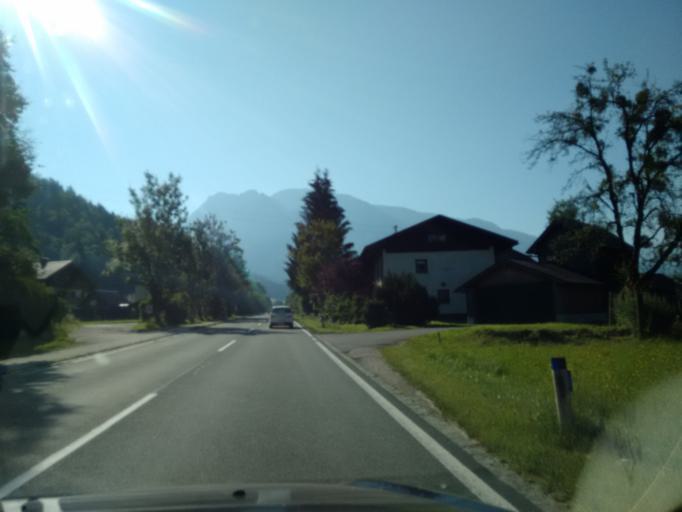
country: AT
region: Upper Austria
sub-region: Politischer Bezirk Gmunden
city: Bad Goisern
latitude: 47.6296
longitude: 13.6341
